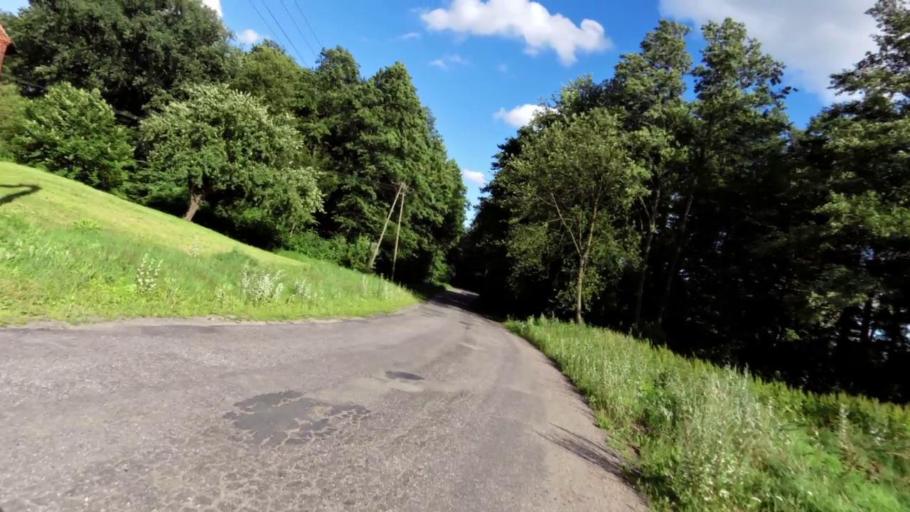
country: PL
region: West Pomeranian Voivodeship
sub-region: Powiat slawienski
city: Slawno
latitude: 54.4353
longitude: 16.7664
